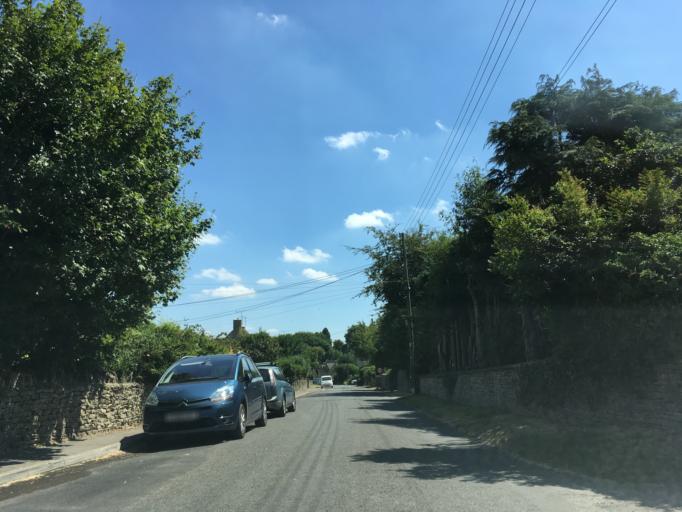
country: GB
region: England
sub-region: Gloucestershire
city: Chalford
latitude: 51.7545
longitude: -2.1437
